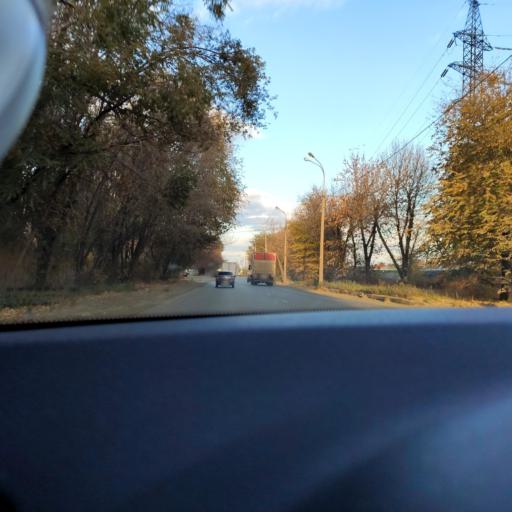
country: RU
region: Samara
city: Smyshlyayevka
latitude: 53.2250
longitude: 50.2961
